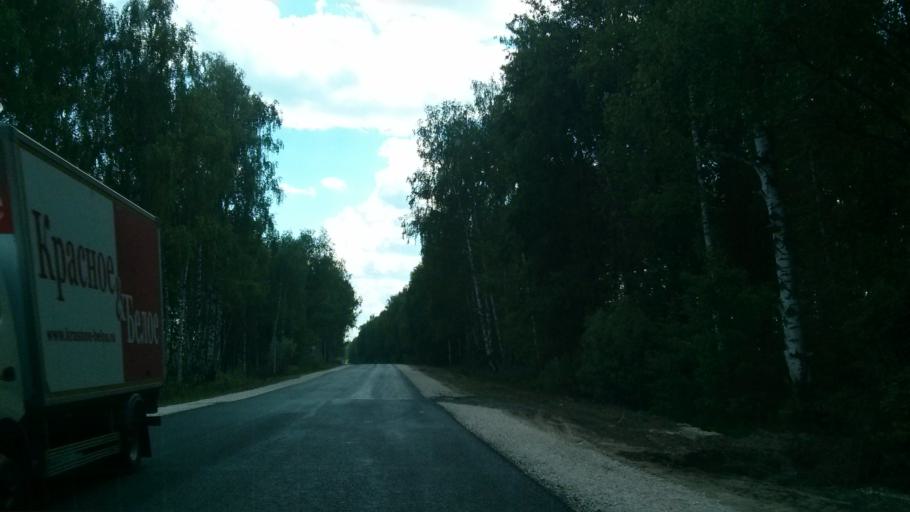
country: RU
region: Vladimir
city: Murom
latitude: 55.5043
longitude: 41.9120
